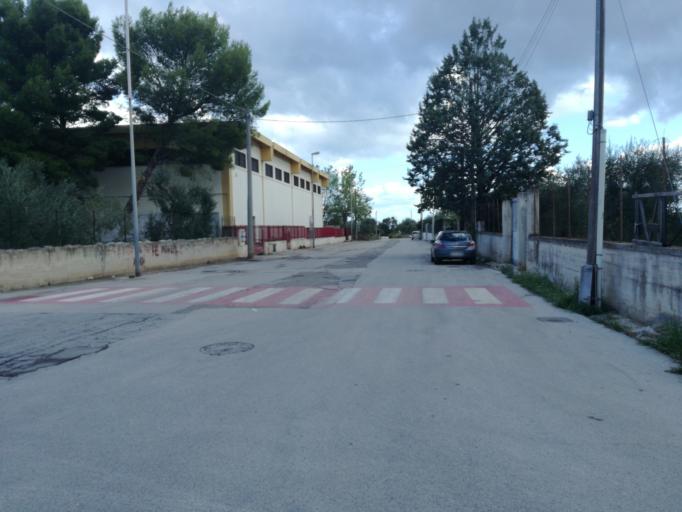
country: IT
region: Apulia
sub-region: Provincia di Bari
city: Triggiano
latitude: 41.0695
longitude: 16.9368
